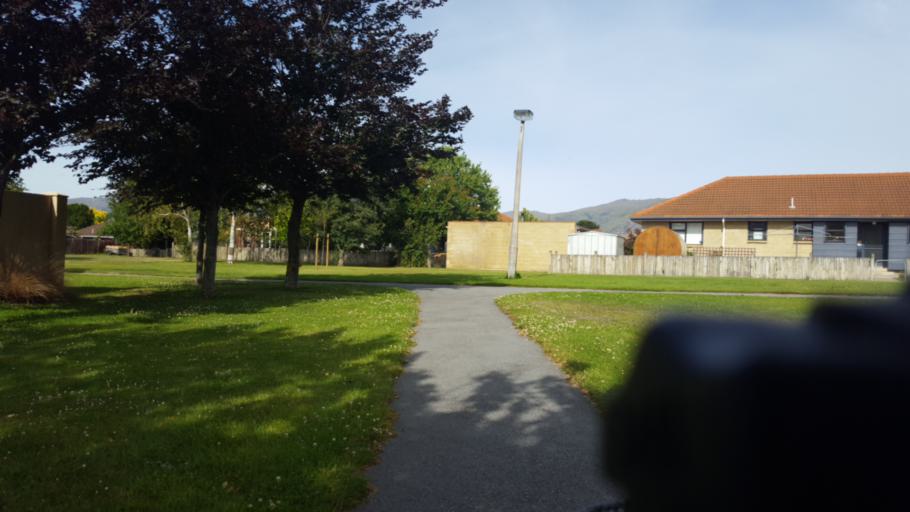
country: NZ
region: Otago
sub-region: Queenstown-Lakes District
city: Wanaka
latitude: -45.0399
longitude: 169.1909
